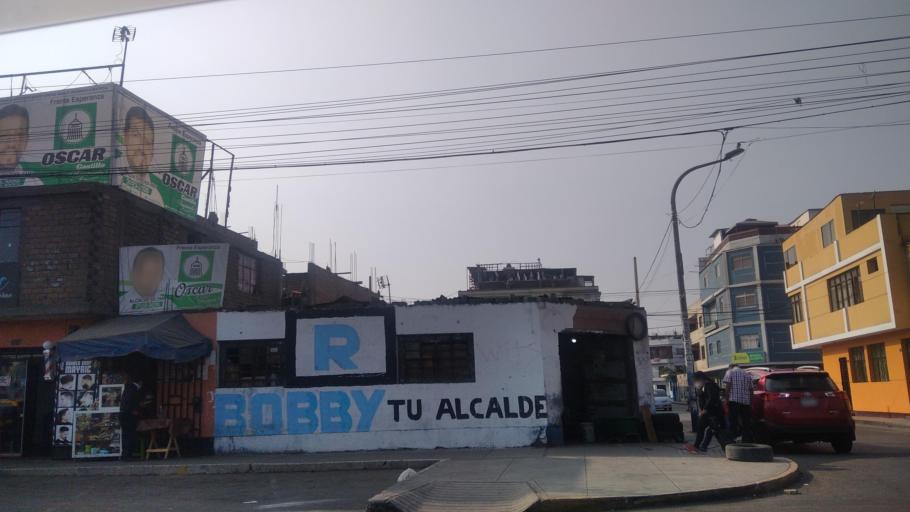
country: PE
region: Lima
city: Lima
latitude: -12.0324
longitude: -77.0626
